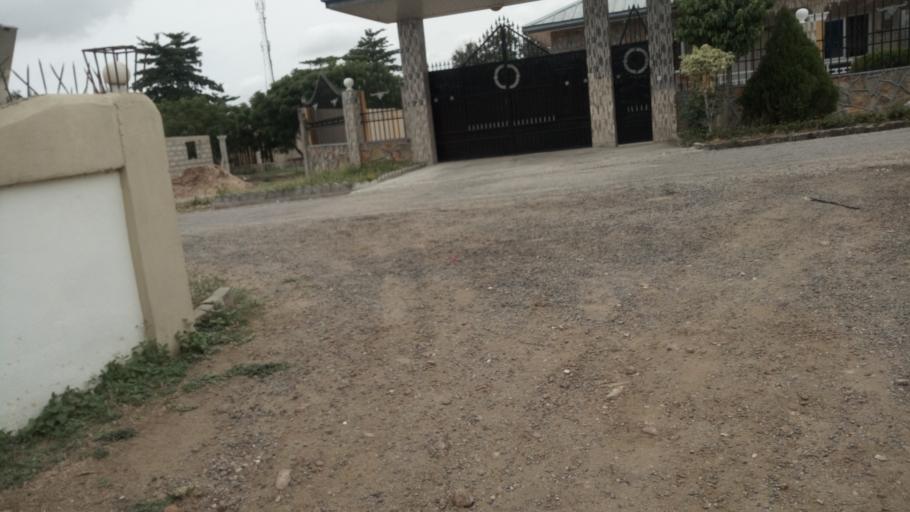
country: GH
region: Central
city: Winneba
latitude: 5.3684
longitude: -0.6411
